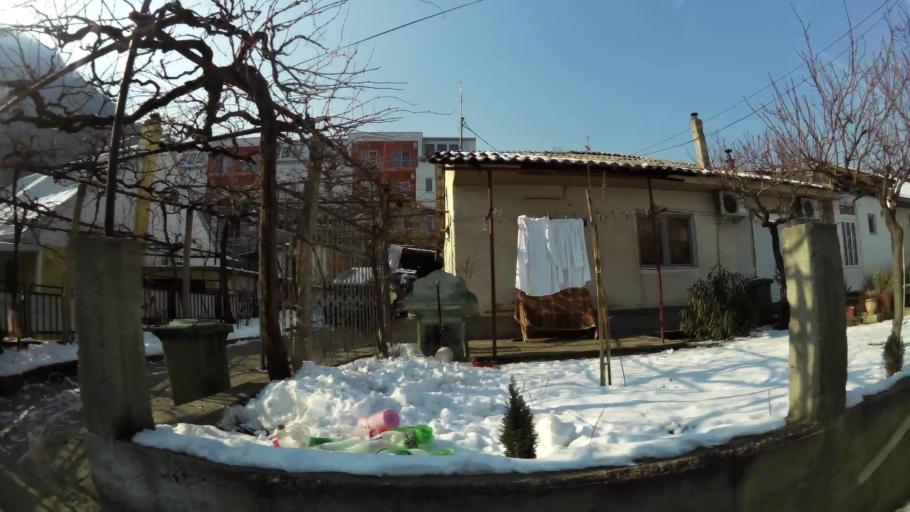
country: MK
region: Sopiste
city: Sopishte
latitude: 41.9729
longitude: 21.4349
